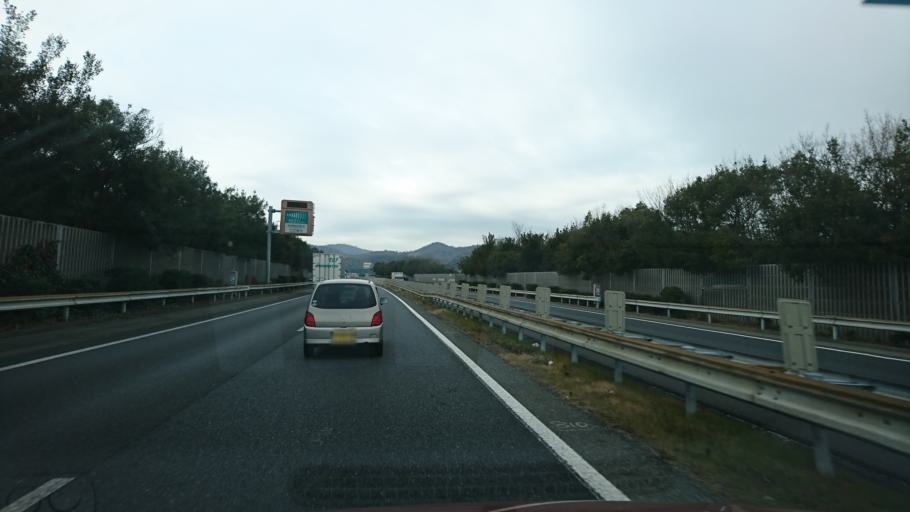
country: JP
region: Okayama
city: Kamogatacho-kamogata
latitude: 34.5518
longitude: 133.5818
